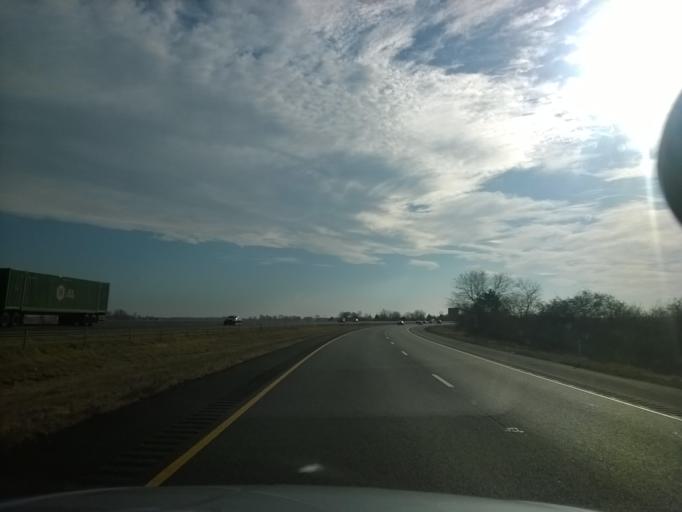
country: US
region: Indiana
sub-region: Johnson County
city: Edinburgh
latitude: 39.3270
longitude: -85.9421
